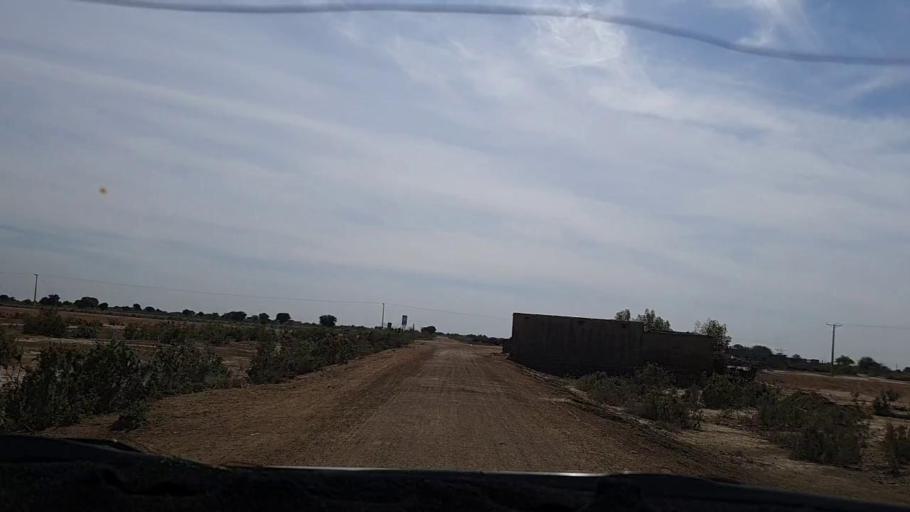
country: PK
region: Sindh
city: Pithoro
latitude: 25.4918
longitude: 69.4564
